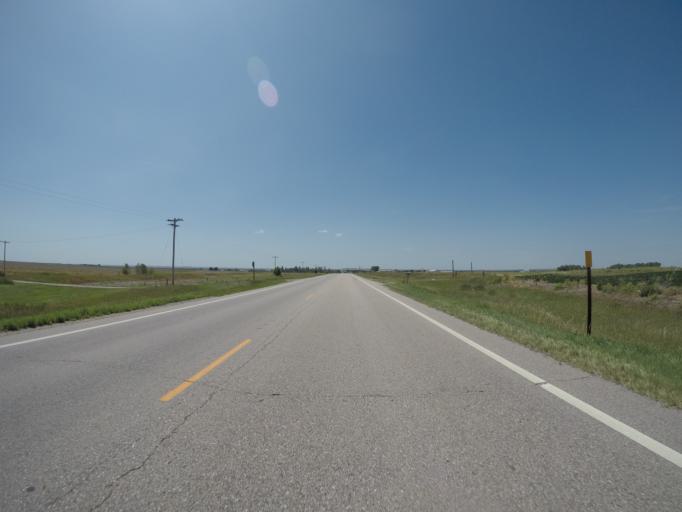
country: US
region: Kansas
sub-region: Osborne County
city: Osborne
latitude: 39.4605
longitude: -98.6947
